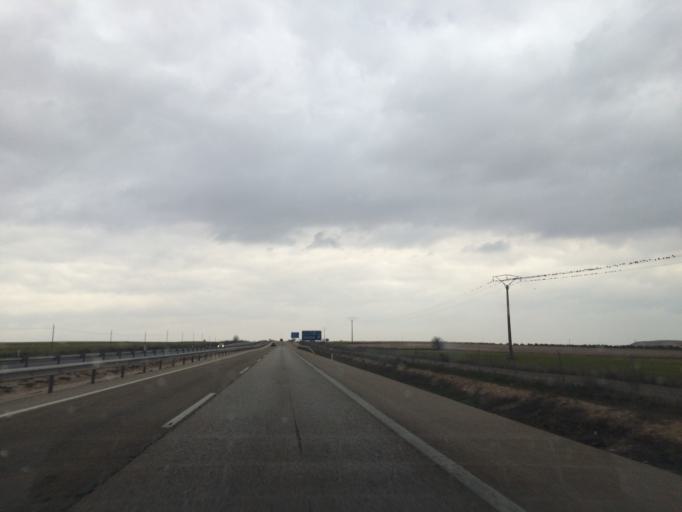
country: ES
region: Castille-La Mancha
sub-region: Province of Toledo
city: Tembleque
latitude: 39.7501
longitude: -3.4851
